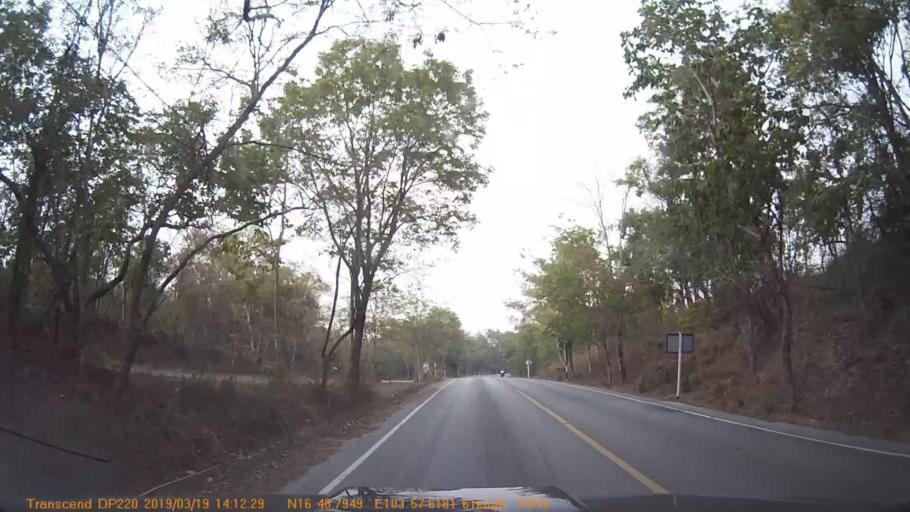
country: TH
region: Kalasin
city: Na Khu
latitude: 16.8137
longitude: 103.9600
